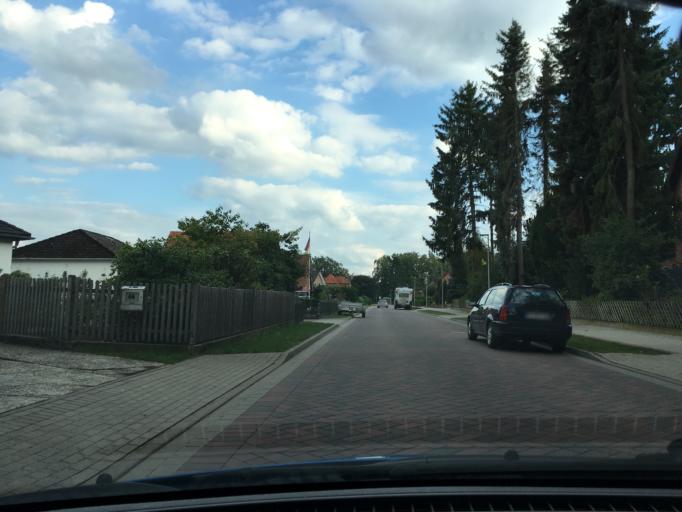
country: DE
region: Lower Saxony
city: Wulfsen
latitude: 53.2908
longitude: 10.1497
